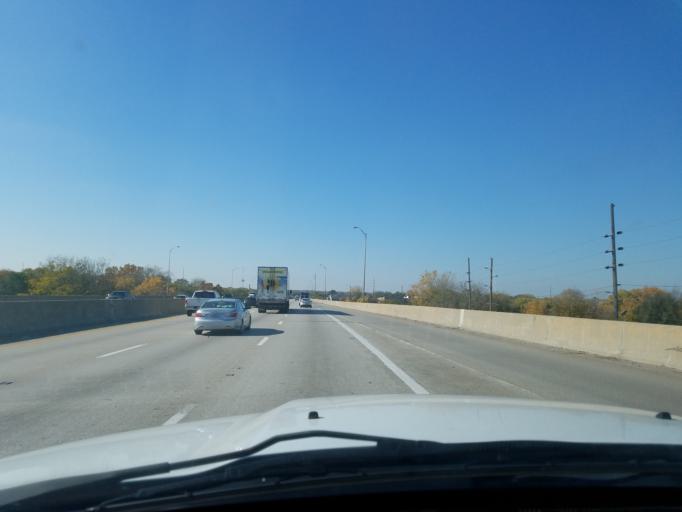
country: US
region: Indiana
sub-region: Marion County
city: Indianapolis
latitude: 39.7544
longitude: -86.1709
